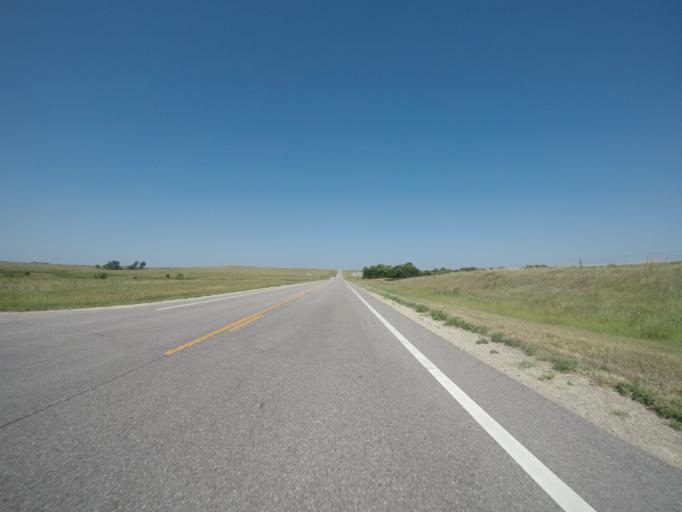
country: US
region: Kansas
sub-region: Cloud County
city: Concordia
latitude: 39.3645
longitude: -97.4536
